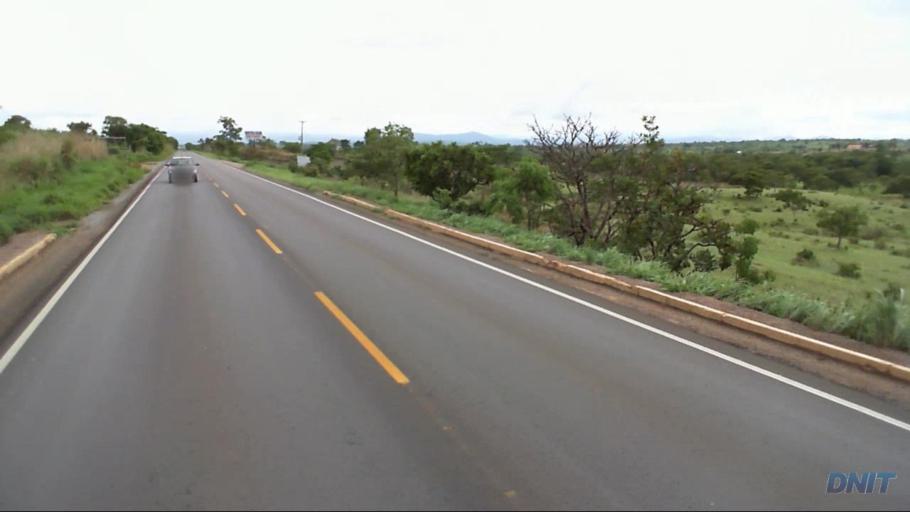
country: BR
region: Goias
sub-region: Padre Bernardo
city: Padre Bernardo
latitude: -15.1947
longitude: -48.2841
